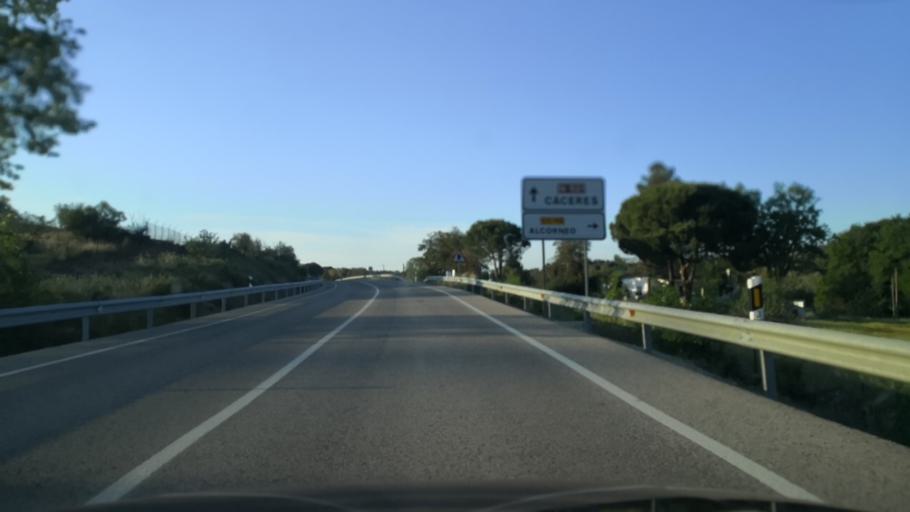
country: ES
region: Extremadura
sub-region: Provincia de Caceres
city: Valencia de Alcantara
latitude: 39.3910
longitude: -7.2463
